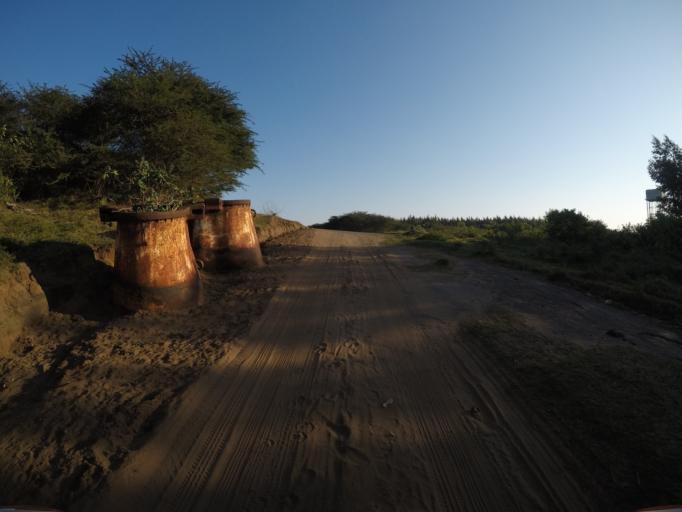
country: ZA
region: KwaZulu-Natal
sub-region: uThungulu District Municipality
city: KwaMbonambi
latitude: -28.7081
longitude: 32.1843
